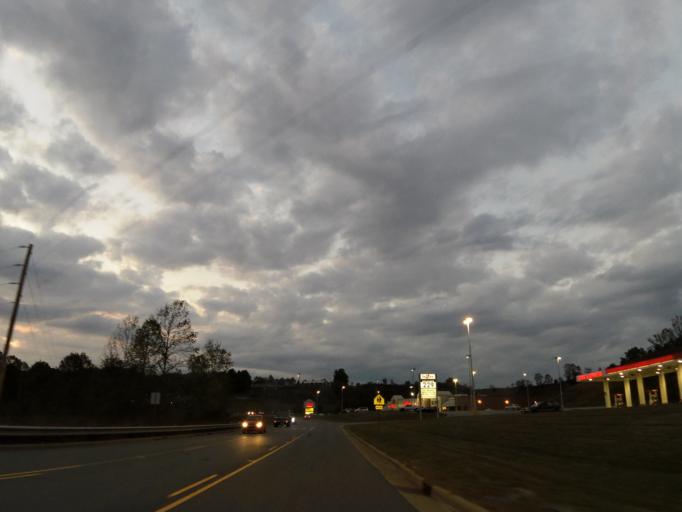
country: US
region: North Carolina
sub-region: Madison County
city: Marshall
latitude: 35.8107
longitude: -82.6705
